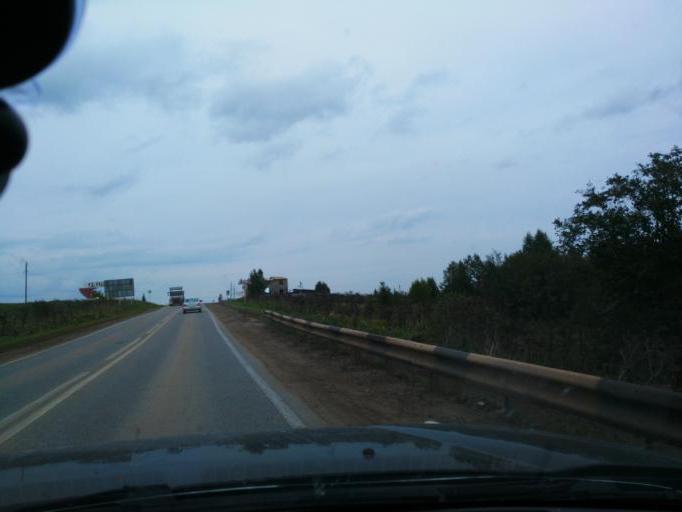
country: RU
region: Perm
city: Chernushka
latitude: 56.5431
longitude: 56.1021
